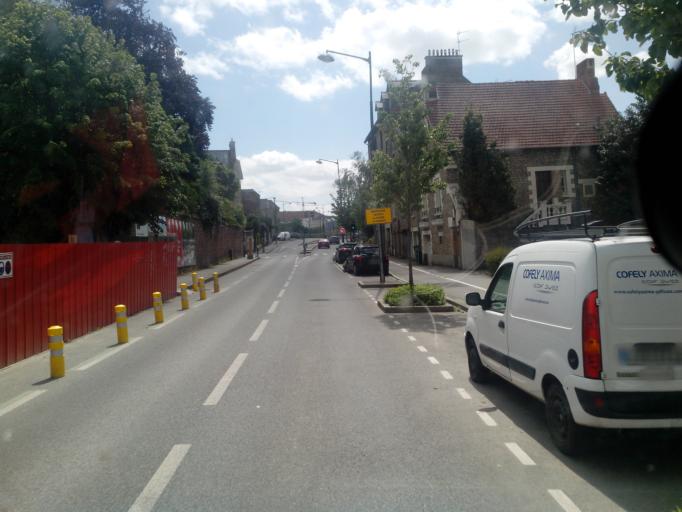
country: FR
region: Brittany
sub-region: Departement d'Ille-et-Vilaine
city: Rennes
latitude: 48.1044
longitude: -1.6937
